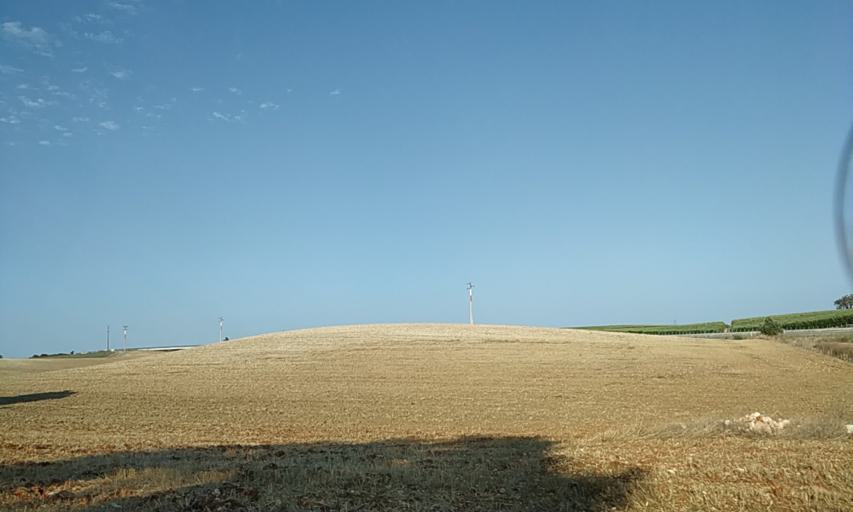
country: PT
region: Santarem
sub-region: Santarem
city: Santarem
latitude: 39.3261
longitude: -8.6627
